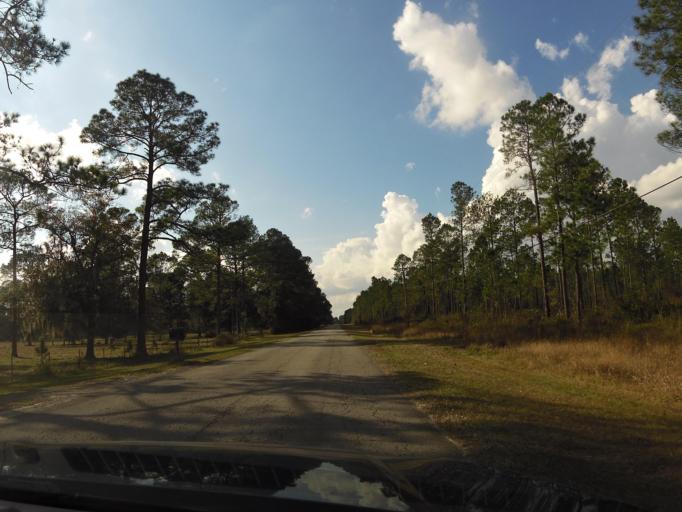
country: US
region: Florida
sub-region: Duval County
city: Baldwin
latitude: 30.1578
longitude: -81.9871
